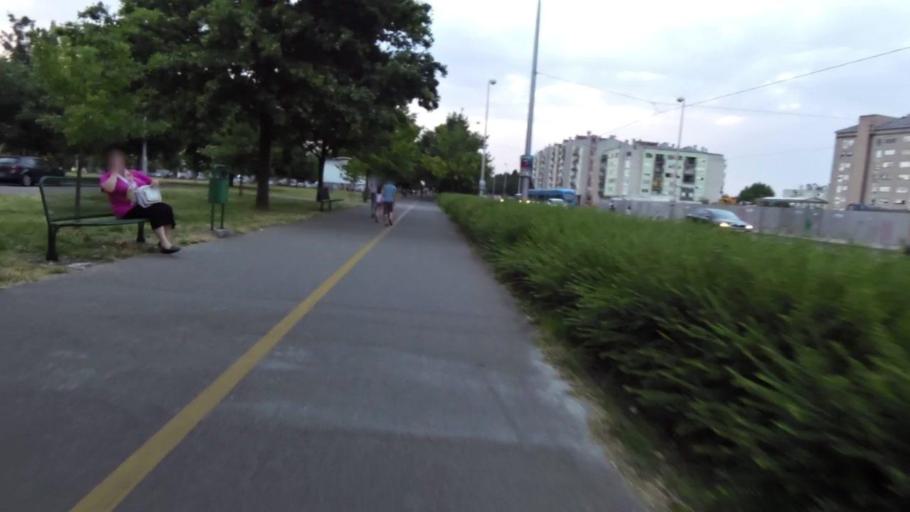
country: HR
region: Grad Zagreb
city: Dubrava
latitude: 45.8289
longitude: 16.0692
